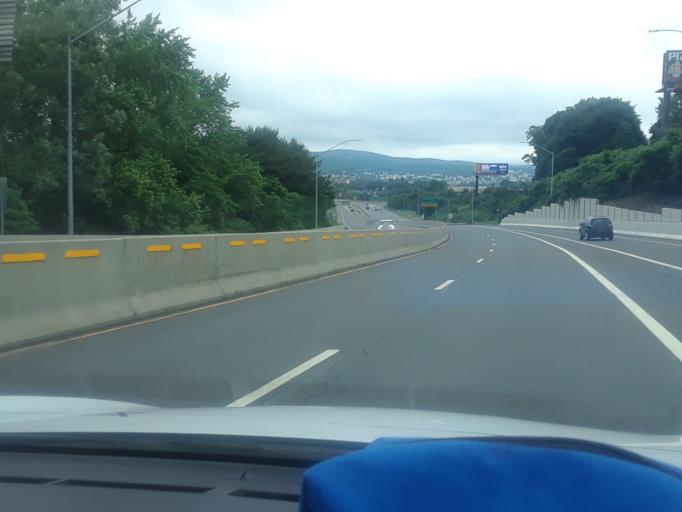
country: US
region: Pennsylvania
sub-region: Lackawanna County
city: Scranton
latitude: 41.4239
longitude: -75.6711
